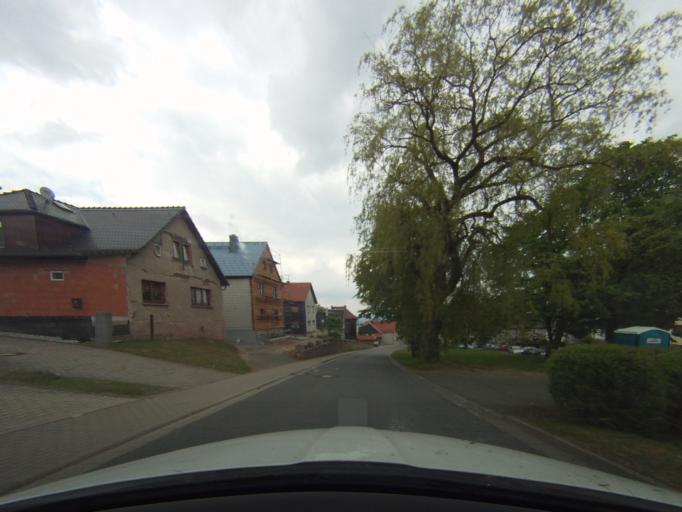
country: DE
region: Thuringia
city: Drobischau
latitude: 50.6407
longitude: 11.0870
